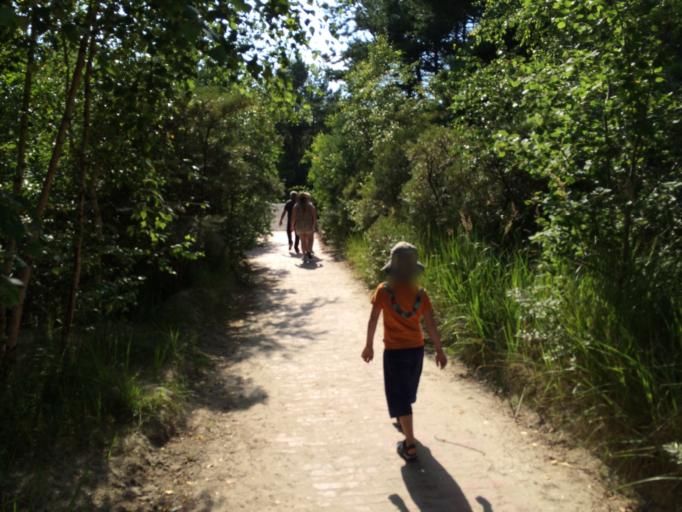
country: DE
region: Mecklenburg-Vorpommern
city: Ostseebad Binz
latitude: 54.4392
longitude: 13.5774
